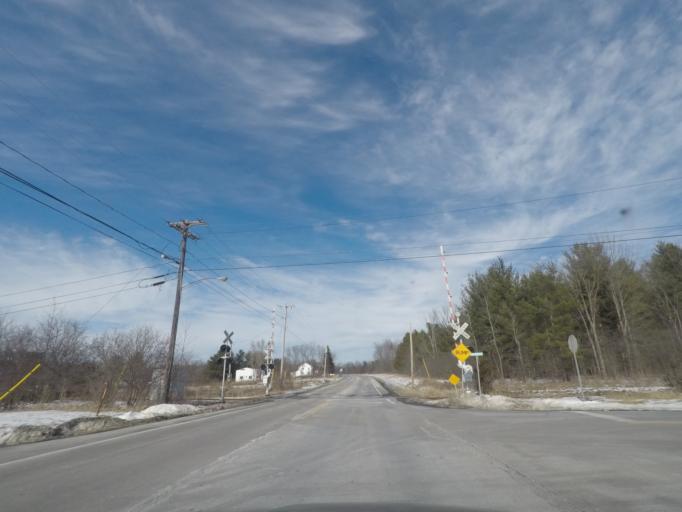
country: US
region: New York
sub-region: Albany County
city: Voorheesville
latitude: 42.6587
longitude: -73.9395
